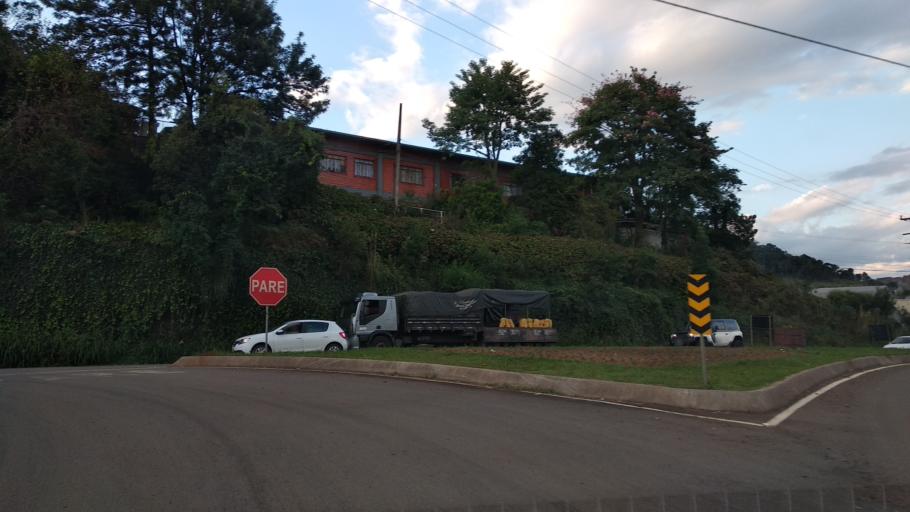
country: BR
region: Santa Catarina
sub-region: Videira
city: Videira
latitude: -26.9985
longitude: -51.1167
